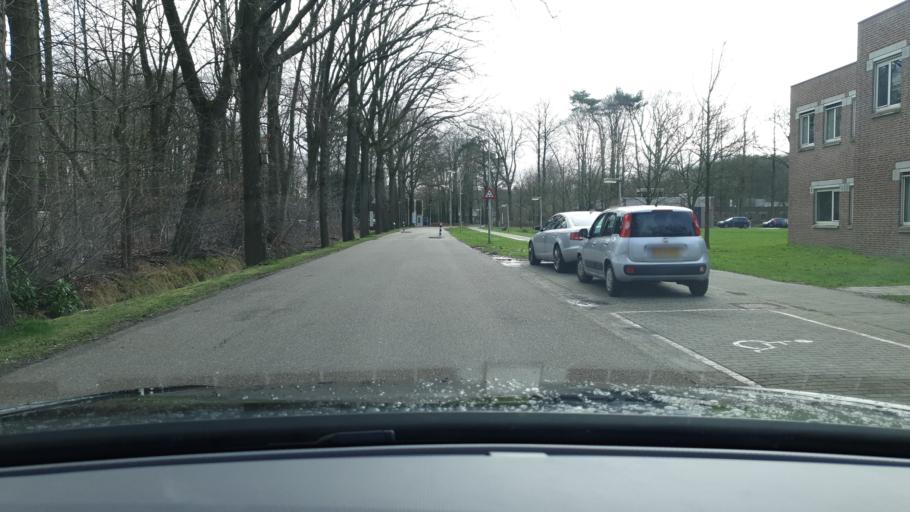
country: NL
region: North Brabant
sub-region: Gemeente Eindhoven
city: Meerhoven
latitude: 51.4699
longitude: 5.4409
